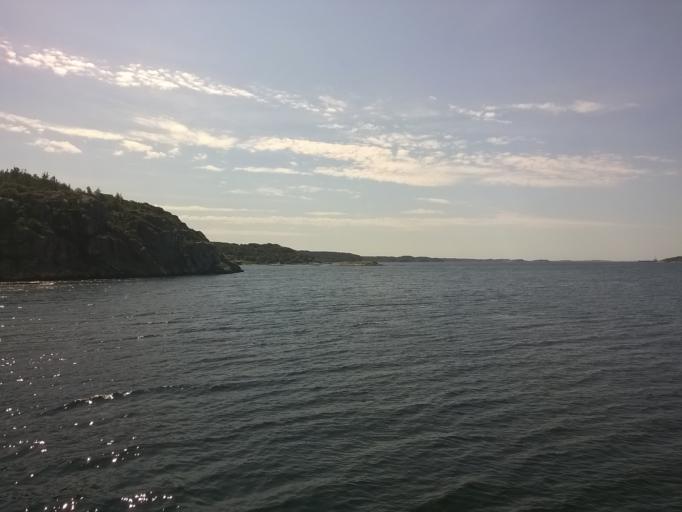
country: SE
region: Vaestra Goetaland
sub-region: Lysekils Kommun
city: Brastad
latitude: 58.3020
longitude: 11.5318
